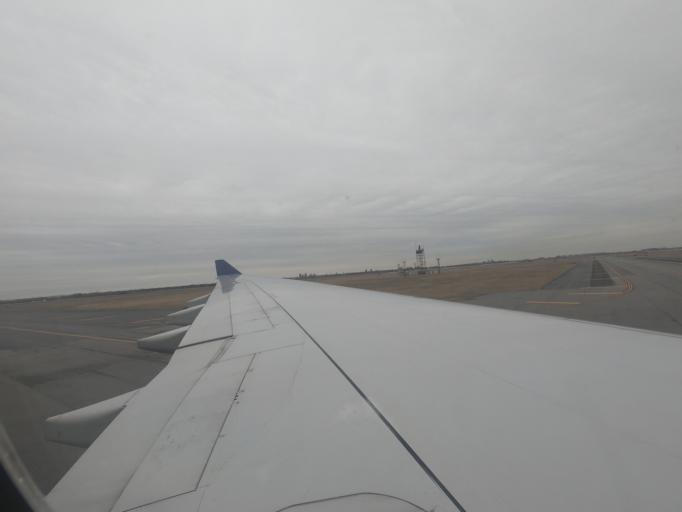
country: US
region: New York
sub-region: Nassau County
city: Inwood
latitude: 40.6426
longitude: -73.7659
